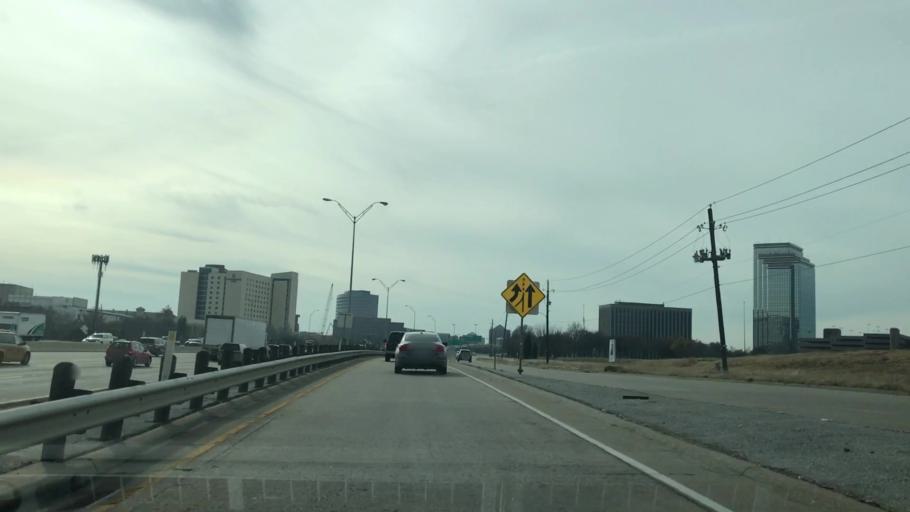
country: US
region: Texas
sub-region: Collin County
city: Plano
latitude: 32.9906
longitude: -96.7105
